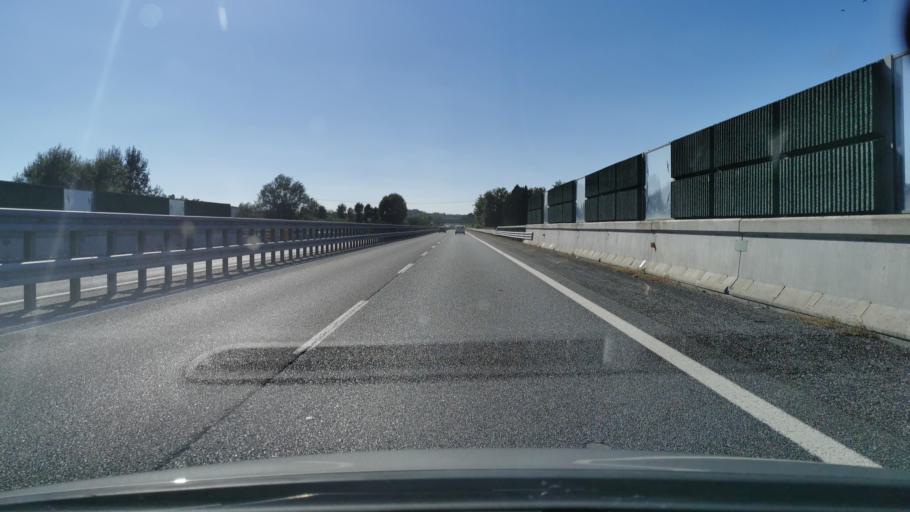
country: IT
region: Piedmont
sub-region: Provincia di Asti
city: Baldichieri d'Asti
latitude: 44.9029
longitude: 8.0894
